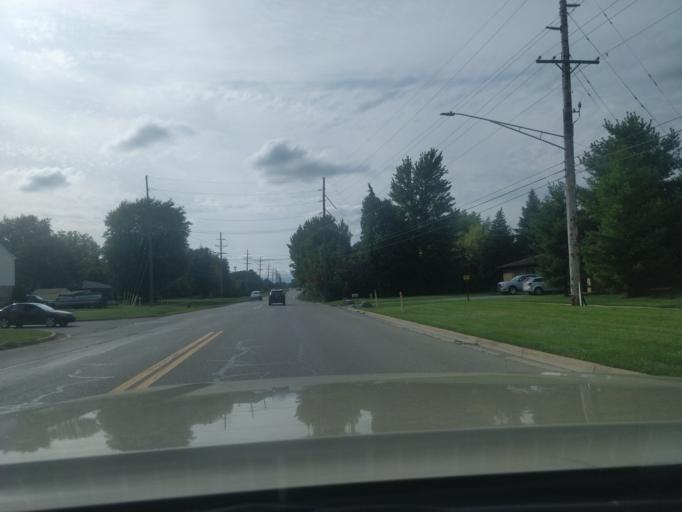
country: US
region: Michigan
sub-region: Wayne County
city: Woodhaven
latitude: 42.1543
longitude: -83.2457
